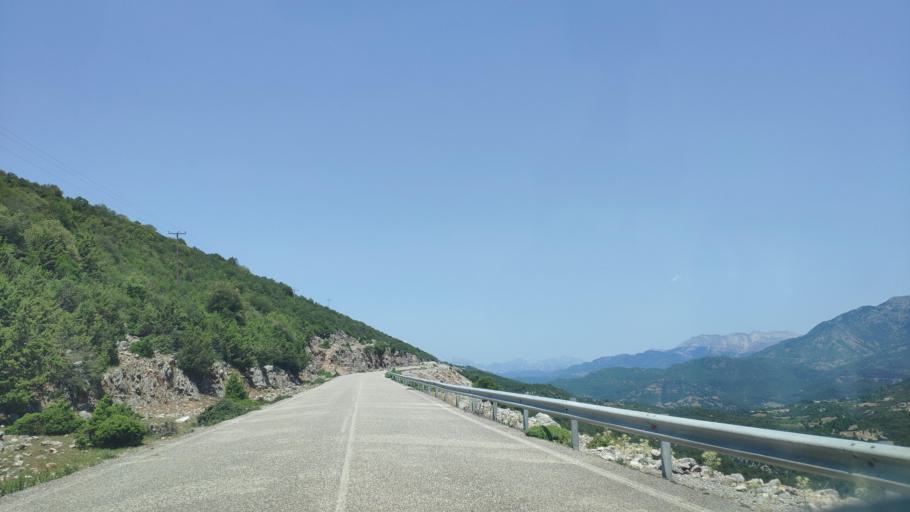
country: GR
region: Thessaly
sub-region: Nomos Kardhitsas
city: Anthiro
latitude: 39.1187
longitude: 21.4039
